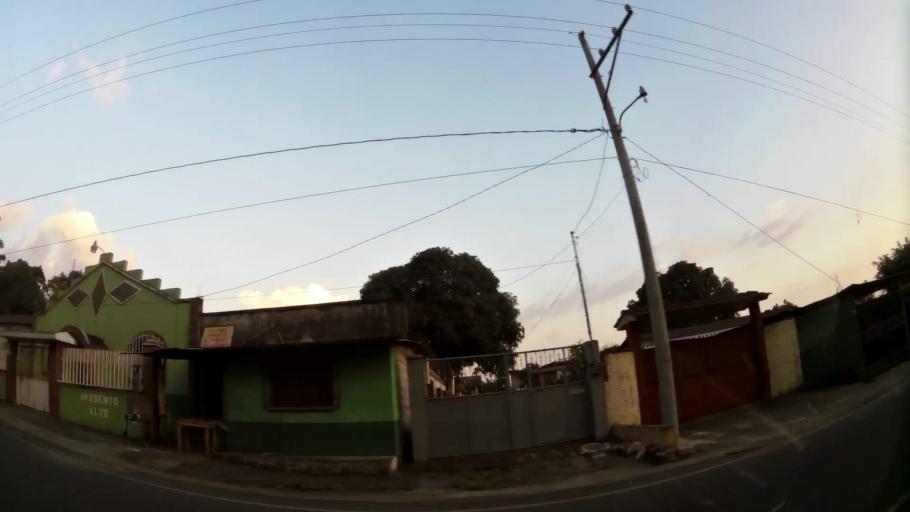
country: GT
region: Retalhuleu
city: Santa Cruz Mulua
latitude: 14.5834
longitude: -91.6230
